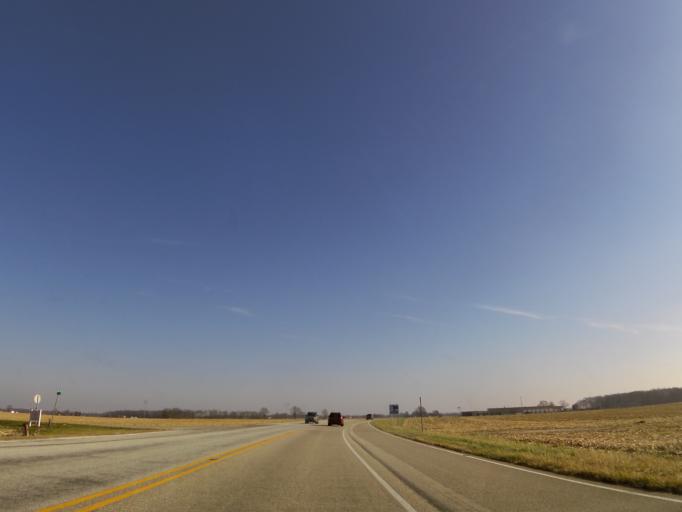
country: US
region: Indiana
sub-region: Shelby County
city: Morristown
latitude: 39.5728
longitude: -85.6110
